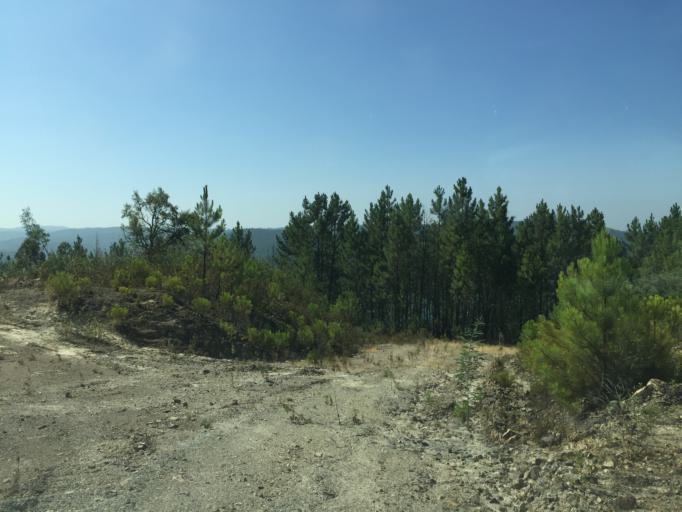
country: PT
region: Santarem
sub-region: Ferreira do Zezere
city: Ferreira do Zezere
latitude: 39.6543
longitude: -8.2387
